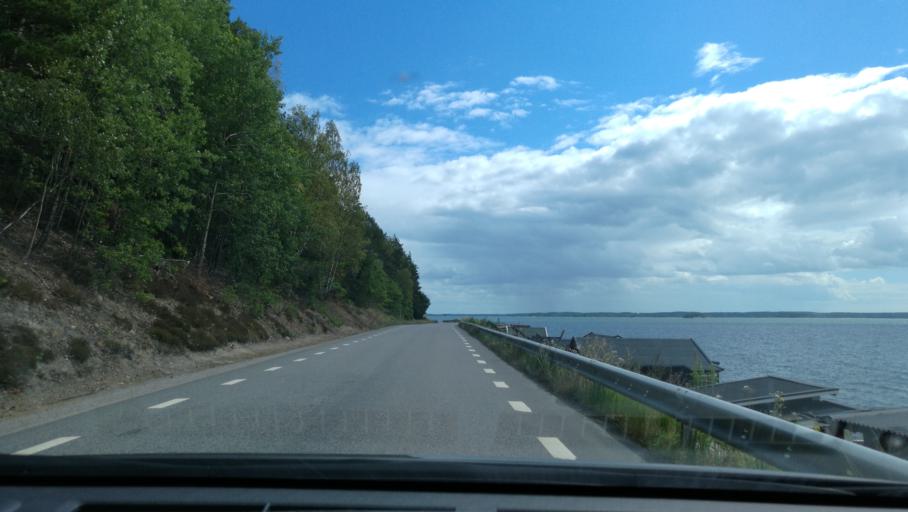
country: SE
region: OEstergoetland
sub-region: Norrkopings Kommun
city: Krokek
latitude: 58.6603
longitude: 16.3753
